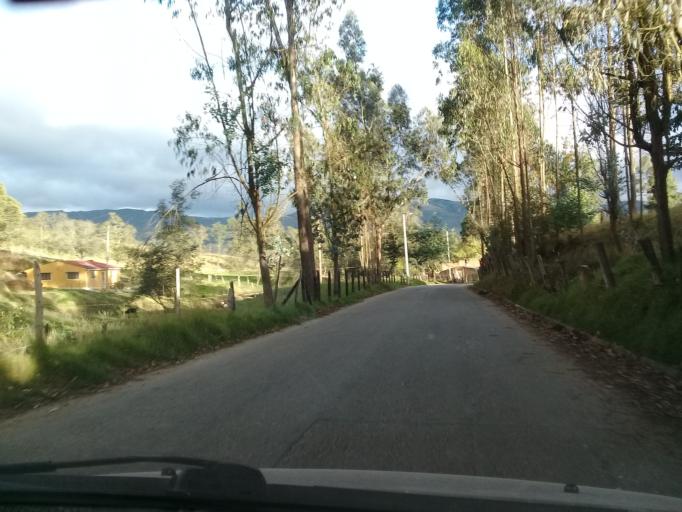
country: CO
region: Cundinamarca
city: Villapinzon
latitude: 5.2217
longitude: -73.6064
